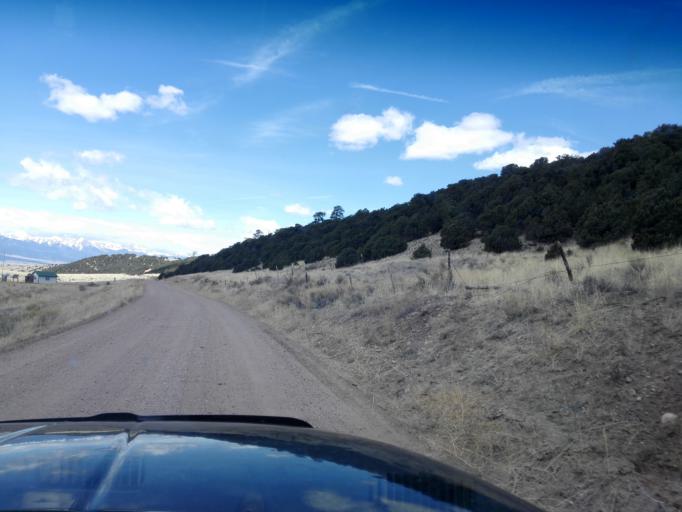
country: US
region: Colorado
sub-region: Custer County
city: Westcliffe
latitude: 37.9804
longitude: -105.2988
